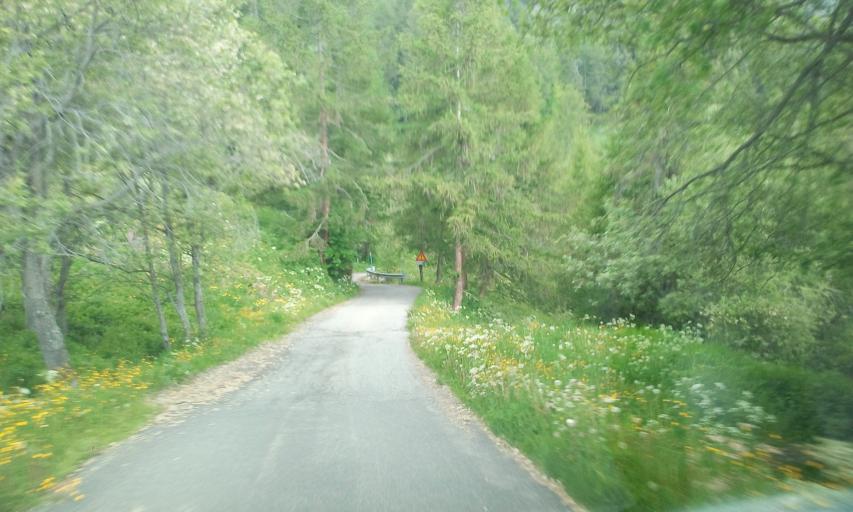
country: IT
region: Aosta Valley
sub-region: Valle d'Aosta
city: Torgnon
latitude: 45.8193
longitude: 7.5766
